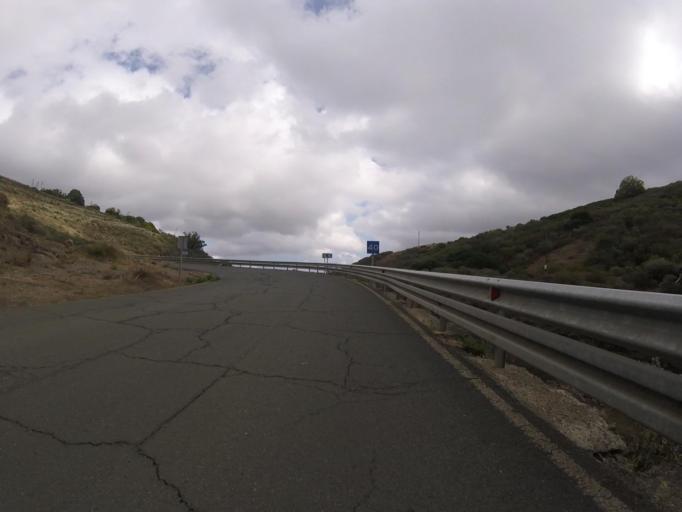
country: ES
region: Canary Islands
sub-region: Provincia de Las Palmas
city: Vega de San Mateo
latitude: 27.9943
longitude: -15.5681
